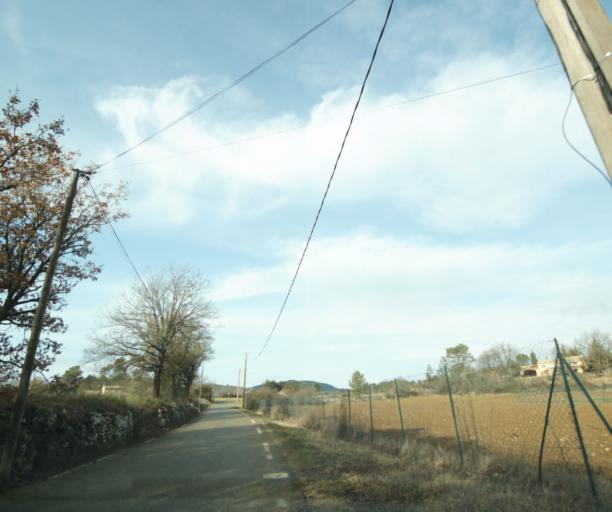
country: FR
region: Provence-Alpes-Cote d'Azur
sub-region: Departement du Var
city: Saint-Maximin-la-Sainte-Baume
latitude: 43.4242
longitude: 5.8668
